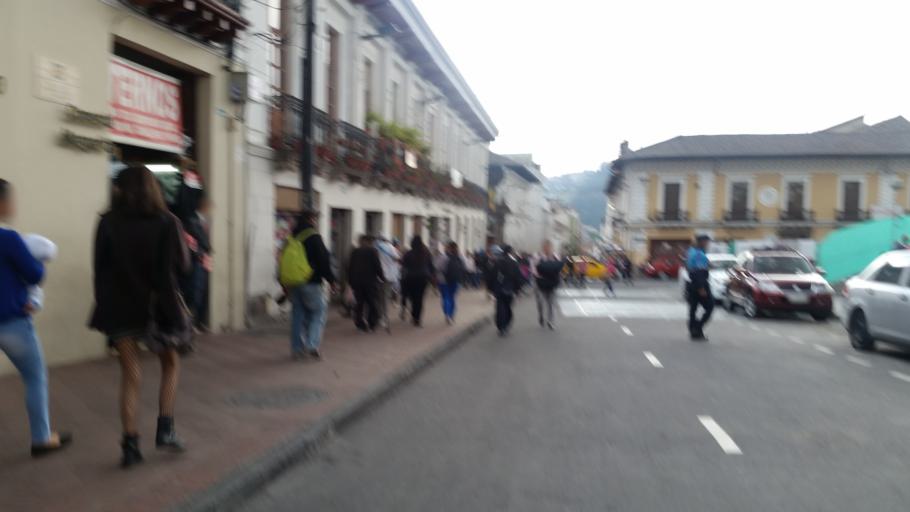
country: EC
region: Pichincha
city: Quito
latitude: -0.2203
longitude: -78.5146
